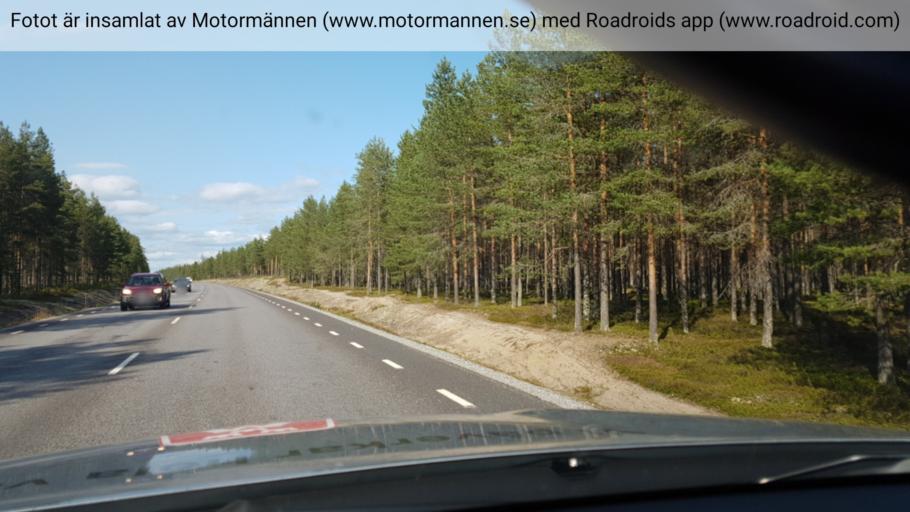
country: SE
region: Norrbotten
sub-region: Pitea Kommun
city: Pitea
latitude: 65.2532
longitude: 21.5376
